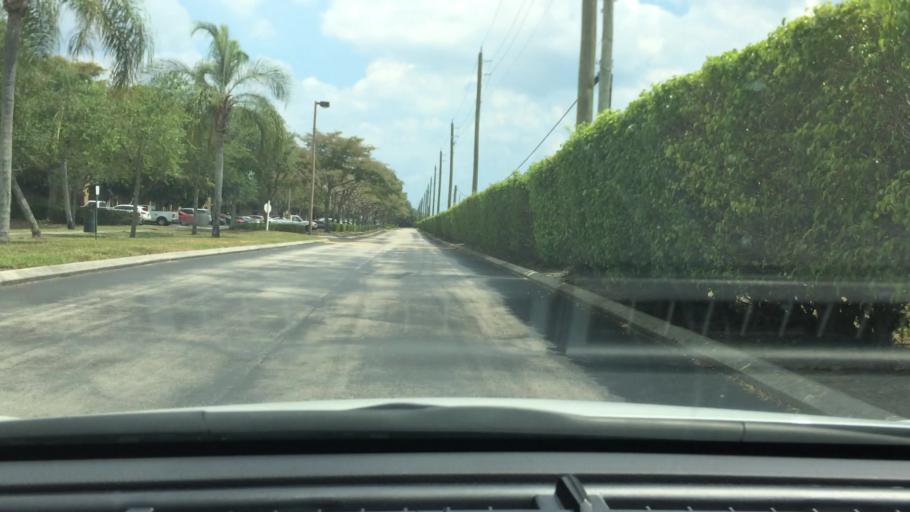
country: US
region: Florida
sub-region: Palm Beach County
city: Villages of Oriole
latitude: 26.5208
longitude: -80.1298
